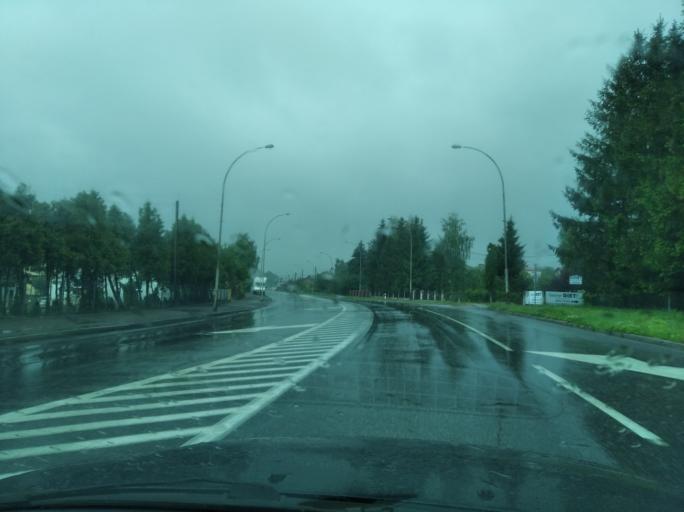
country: PL
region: Subcarpathian Voivodeship
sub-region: Powiat jasielski
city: Jaslo
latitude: 49.7570
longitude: 21.4982
